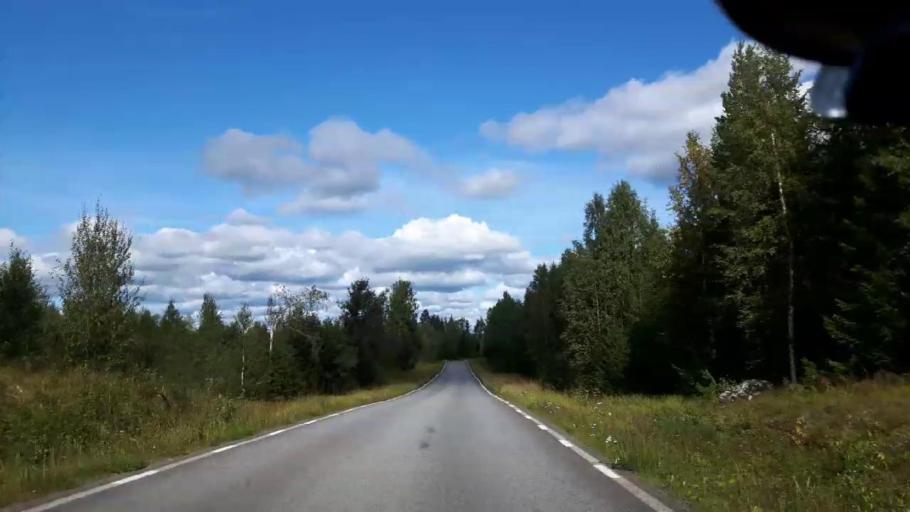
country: SE
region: Jaemtland
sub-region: OEstersunds Kommun
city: Brunflo
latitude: 63.2164
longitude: 15.2445
